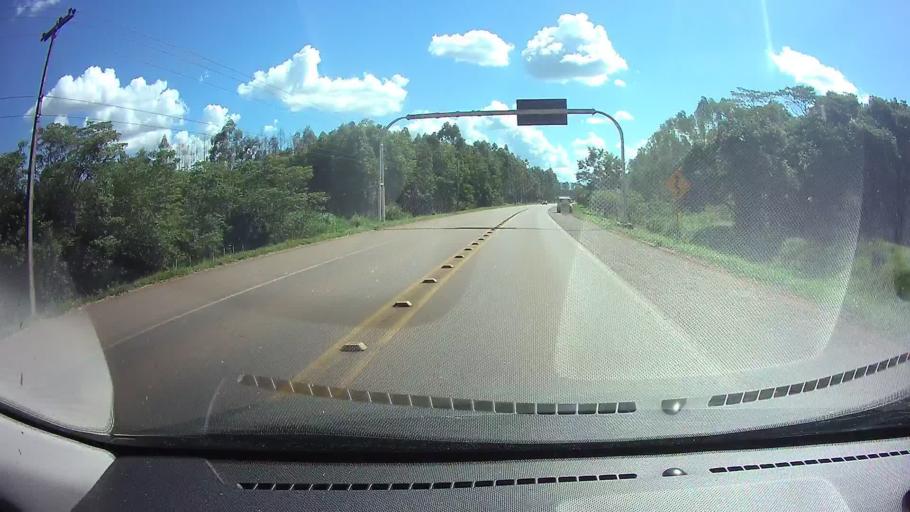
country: PY
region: Guaira
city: Coronel Martinez
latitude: -25.7675
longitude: -56.6560
